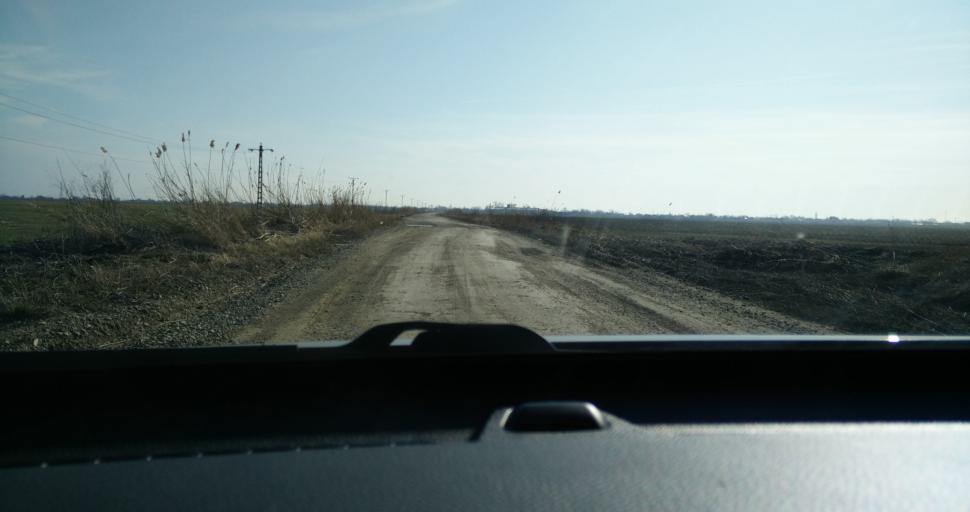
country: RO
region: Vrancea
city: Vulturu de Sus
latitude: 45.6437
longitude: 27.3927
